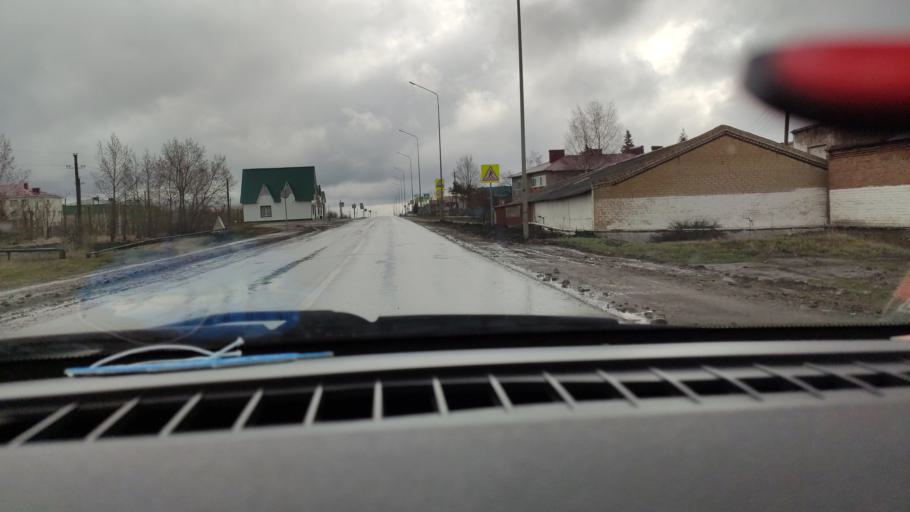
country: RU
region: Tatarstan
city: Nurlat
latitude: 54.4325
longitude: 50.8214
